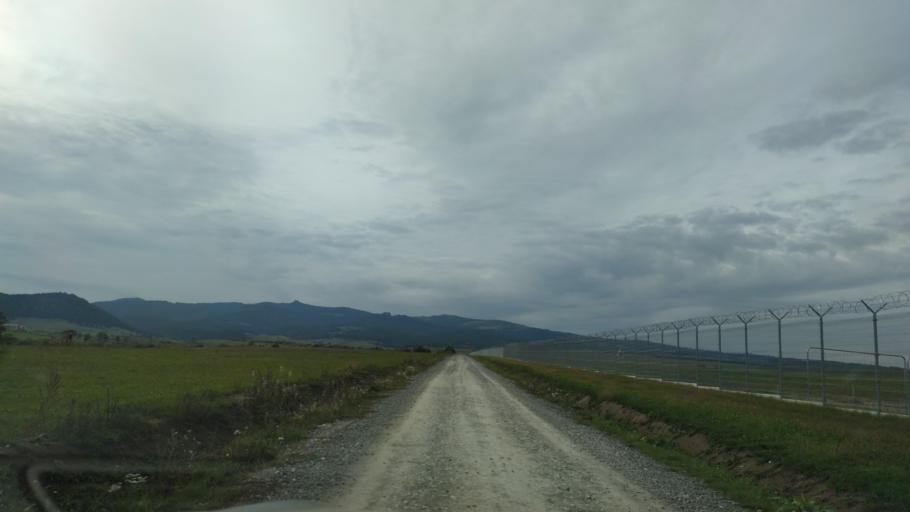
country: RO
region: Harghita
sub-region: Comuna Subcetate
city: Subcetate
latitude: 46.8175
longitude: 25.4117
